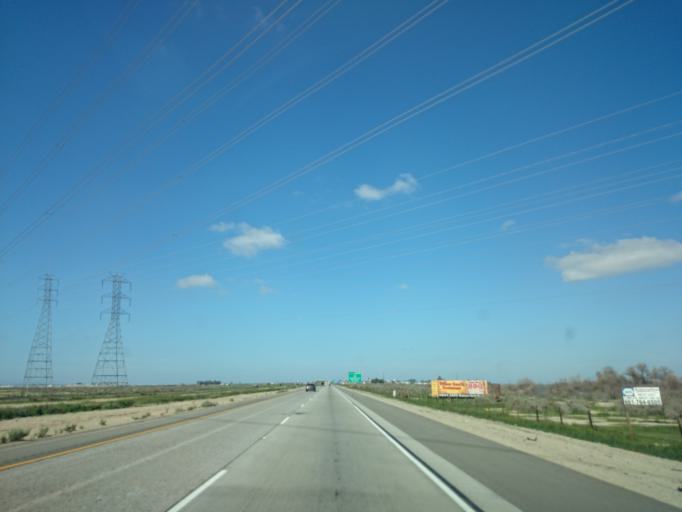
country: US
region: California
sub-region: Kern County
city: Buttonwillow
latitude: 35.3875
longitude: -119.3813
